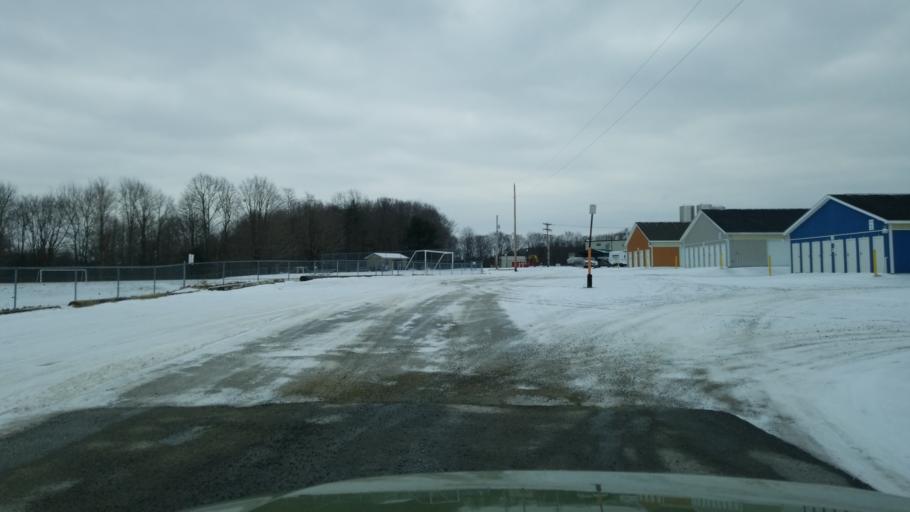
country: US
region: Pennsylvania
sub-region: Clearfield County
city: DuBois
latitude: 41.1086
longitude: -78.7306
